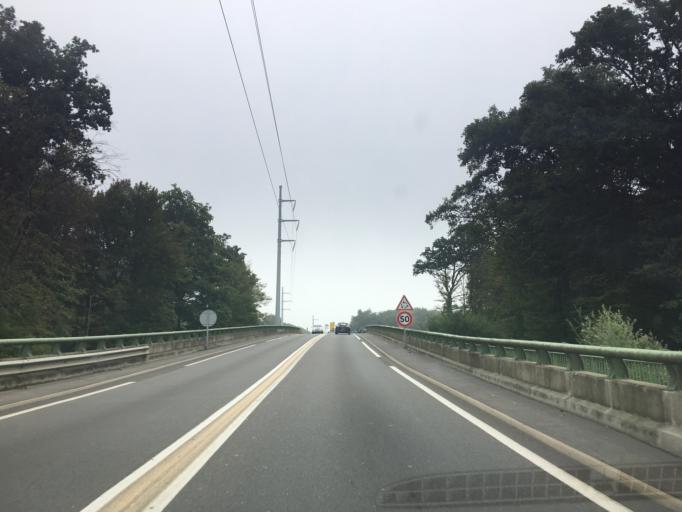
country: FR
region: Ile-de-France
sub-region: Departement de l'Essonne
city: Tigery
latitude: 48.6592
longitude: 2.5158
